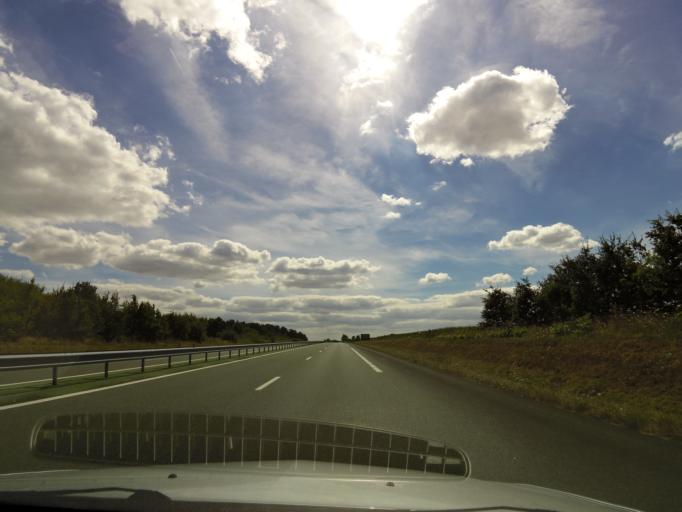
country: FR
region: Pays de la Loire
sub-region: Departement de la Vendee
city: La Ferriere
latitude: 46.7370
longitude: -1.2708
